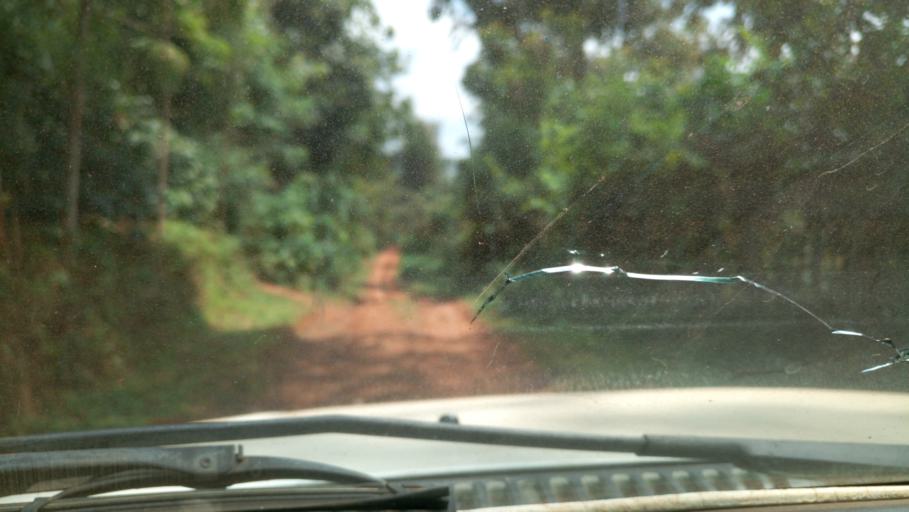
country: KE
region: Murang'a District
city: Maragua
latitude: -0.8168
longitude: 37.0126
